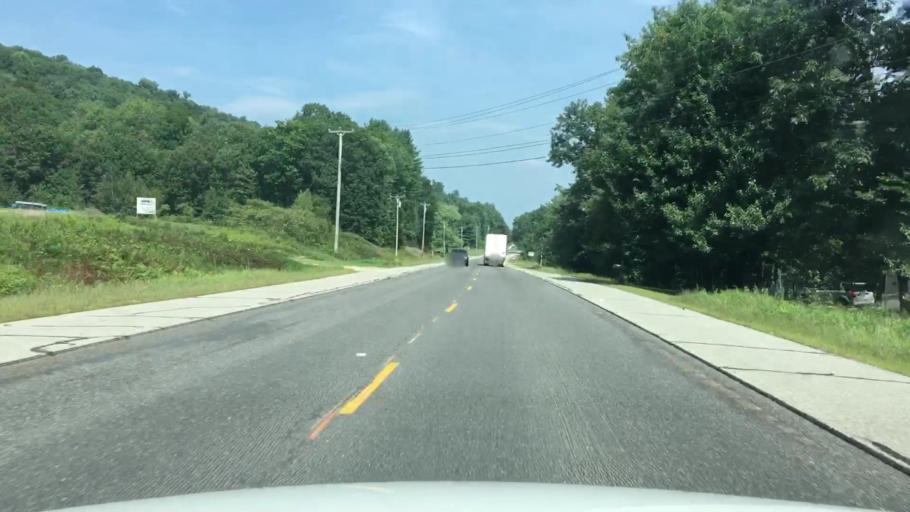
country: US
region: Maine
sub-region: Androscoggin County
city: Turner
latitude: 44.3124
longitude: -70.2646
